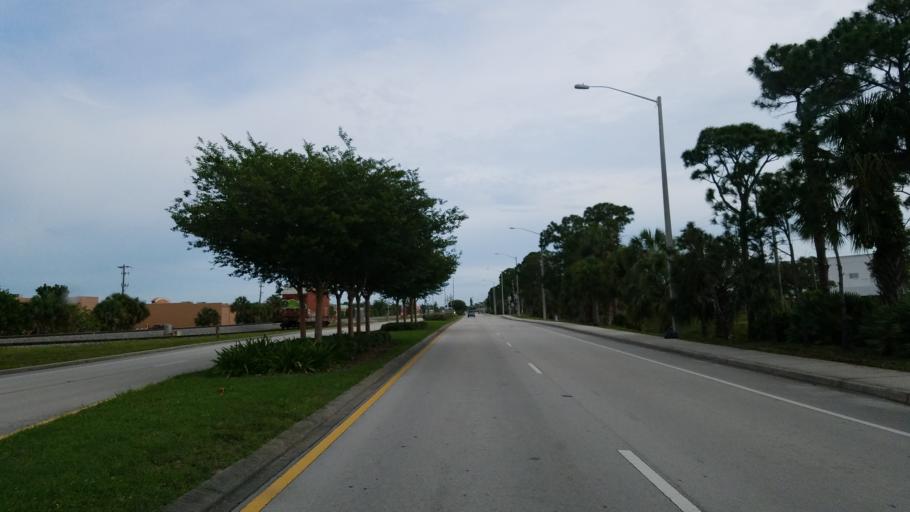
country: US
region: Florida
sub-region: Martin County
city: Stuart
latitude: 27.1764
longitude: -80.2313
